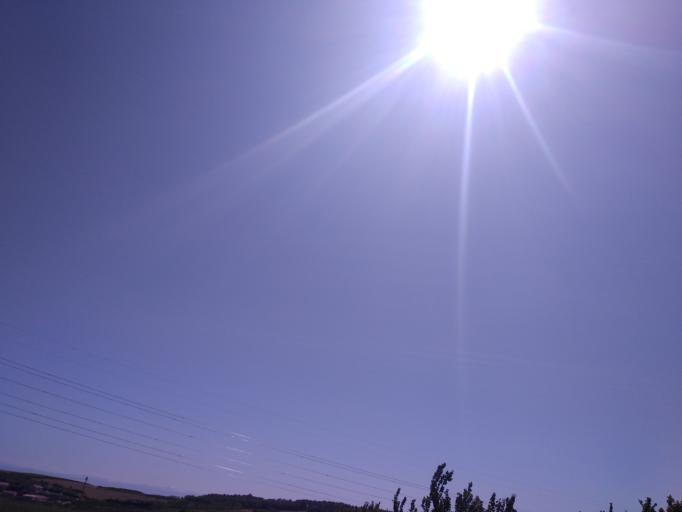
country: FR
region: Rhone-Alpes
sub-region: Departement de l'Ardeche
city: Sarras
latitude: 45.1820
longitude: 4.7506
